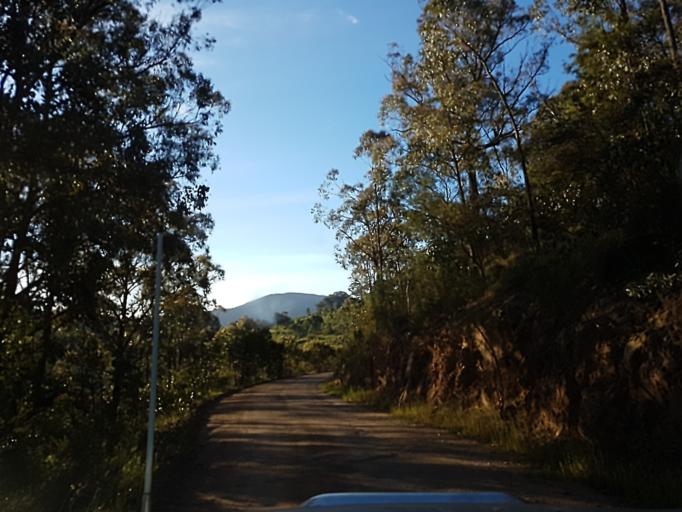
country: AU
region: Victoria
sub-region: East Gippsland
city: Bairnsdale
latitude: -37.4137
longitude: 147.1244
